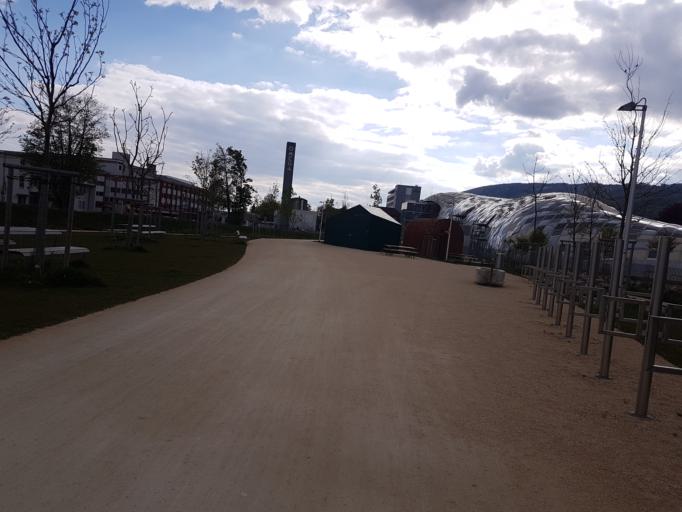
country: CH
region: Bern
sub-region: Biel/Bienne District
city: Biel/Bienne
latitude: 47.1447
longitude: 7.2644
